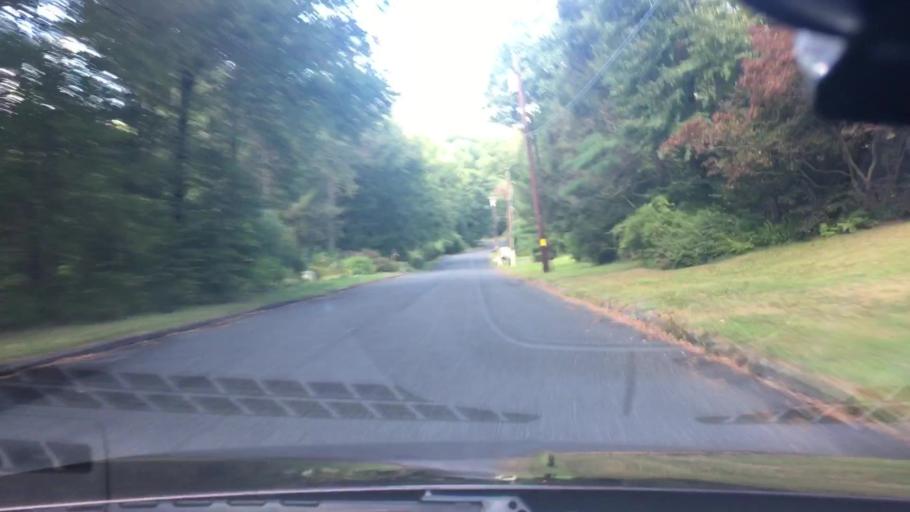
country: US
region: Connecticut
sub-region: Tolland County
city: Somers
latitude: 41.9799
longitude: -72.4120
